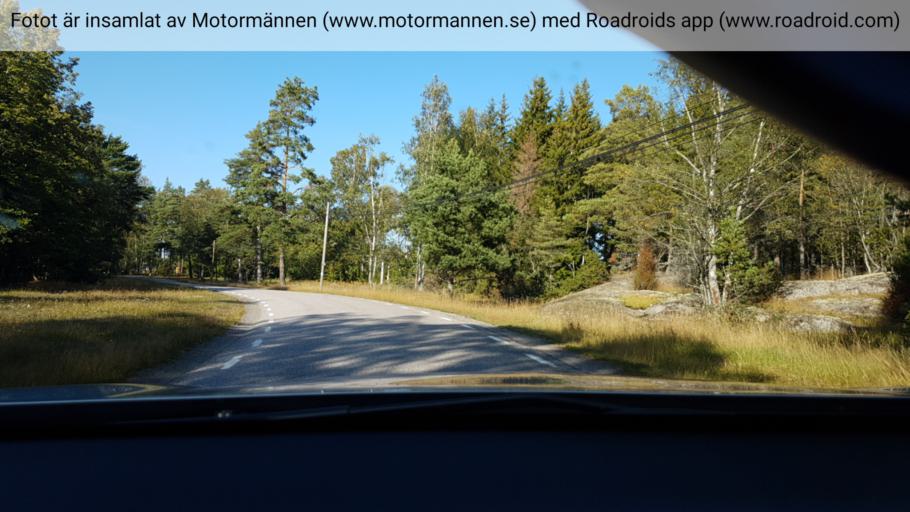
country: SE
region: Stockholm
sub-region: Nynashamns Kommun
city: Nynashamn
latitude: 58.8194
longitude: 17.8346
